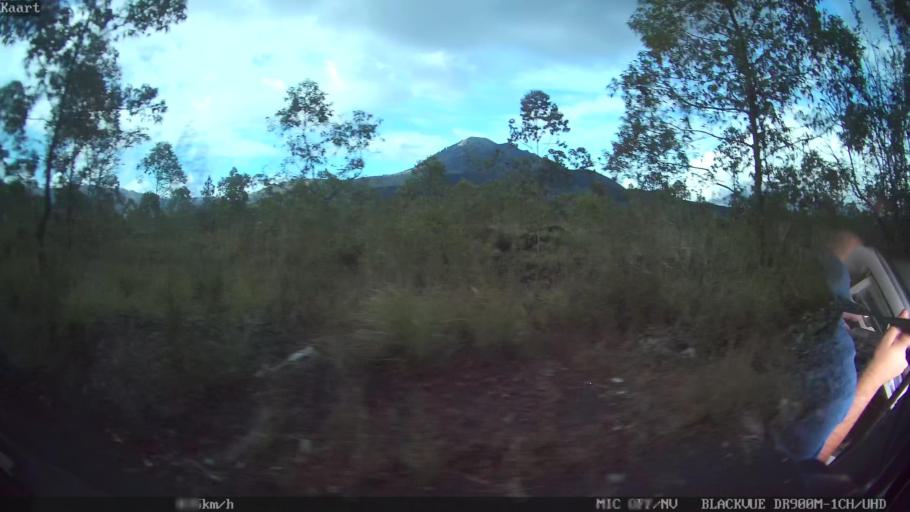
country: ID
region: Bali
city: Banjar Kedisan
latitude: -8.2513
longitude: 115.3488
